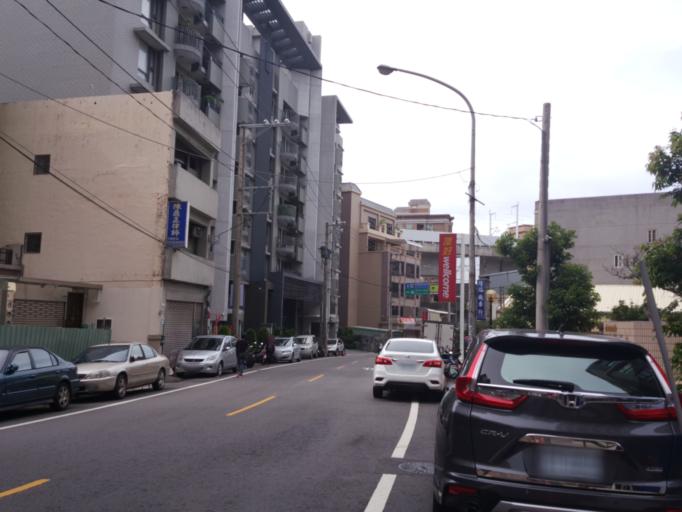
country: TW
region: Taiwan
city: Taoyuan City
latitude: 25.0600
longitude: 121.2971
